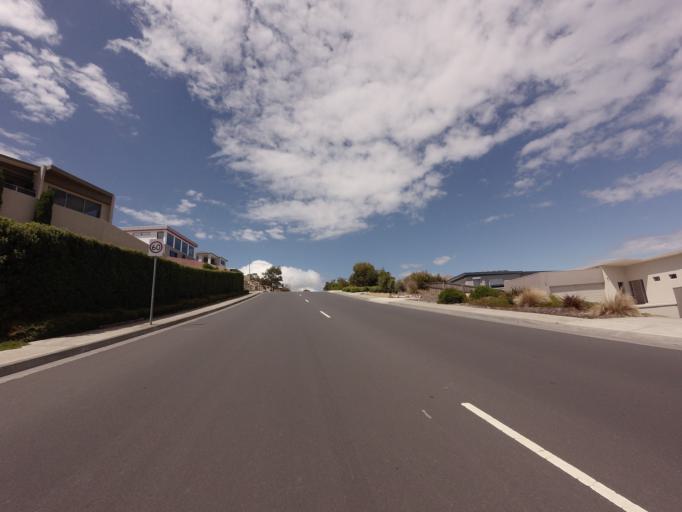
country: AU
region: Tasmania
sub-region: Clarence
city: Howrah
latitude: -42.8988
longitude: 147.4167
